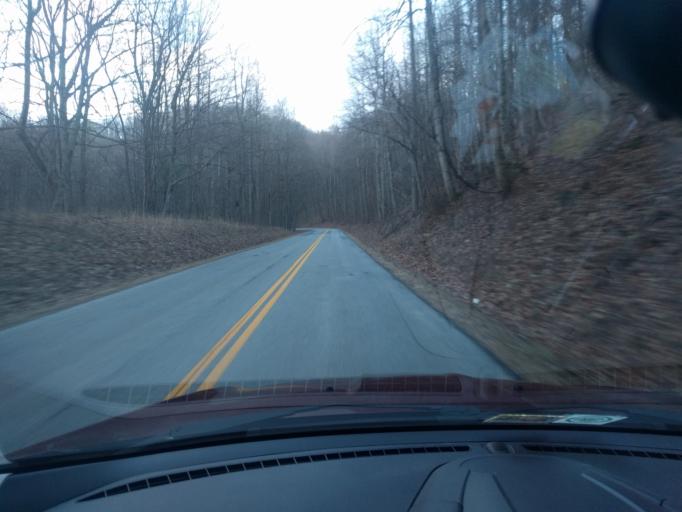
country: US
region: Virginia
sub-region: Botetourt County
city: Buchanan
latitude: 37.4690
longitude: -79.6381
